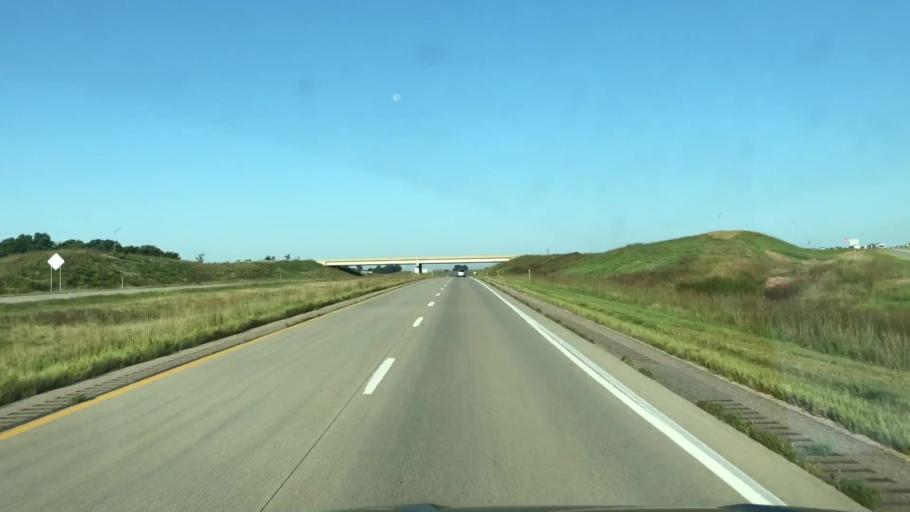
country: US
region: Iowa
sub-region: Plymouth County
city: Le Mars
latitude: 42.8187
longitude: -96.1709
